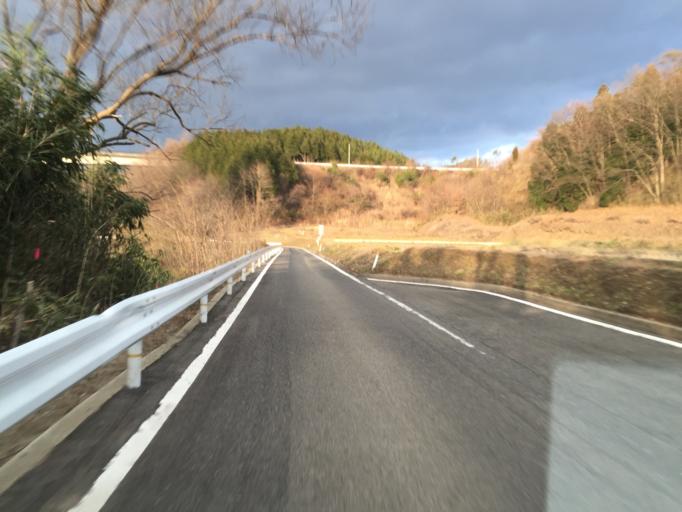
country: JP
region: Fukushima
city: Motomiya
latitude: 37.5334
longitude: 140.4158
